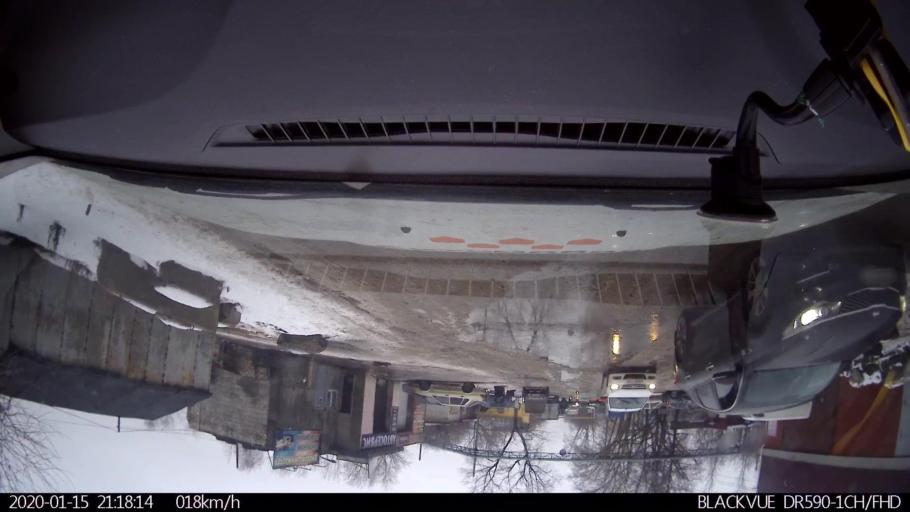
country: RU
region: Nizjnij Novgorod
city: Gorbatovka
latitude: 56.3008
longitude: 43.8611
